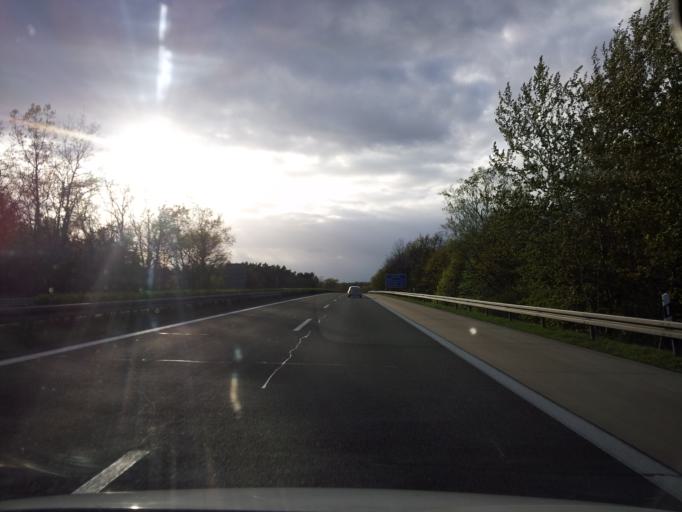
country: DE
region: Brandenburg
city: Lubbenau
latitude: 51.8346
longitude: 13.9718
